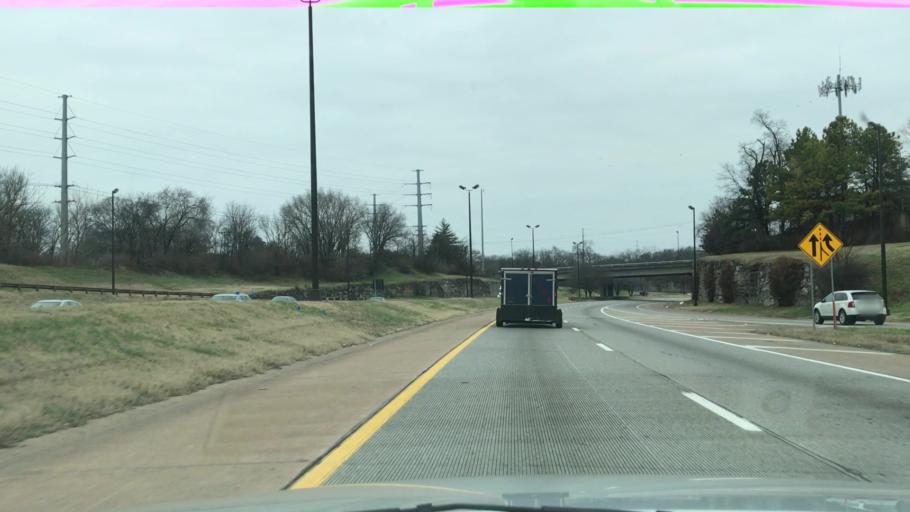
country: US
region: Tennessee
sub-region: Davidson County
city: Nashville
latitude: 36.1377
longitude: -86.8219
